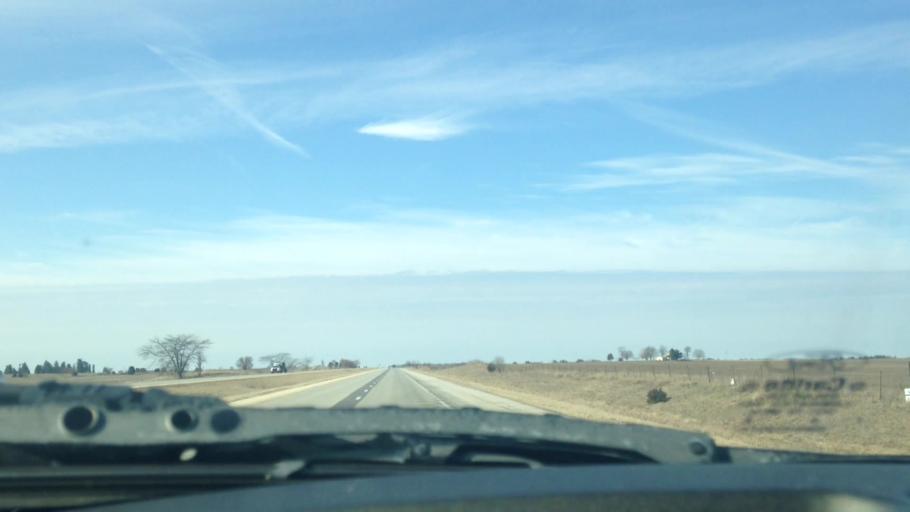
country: US
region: Illinois
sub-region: Ford County
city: Paxton
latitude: 40.5385
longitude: -88.0704
